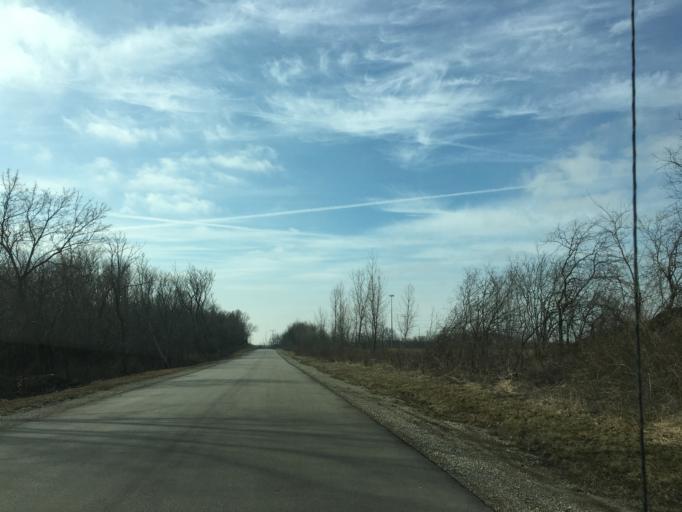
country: US
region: Illinois
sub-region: Kane County
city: East Dundee
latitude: 42.0882
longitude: -88.2338
